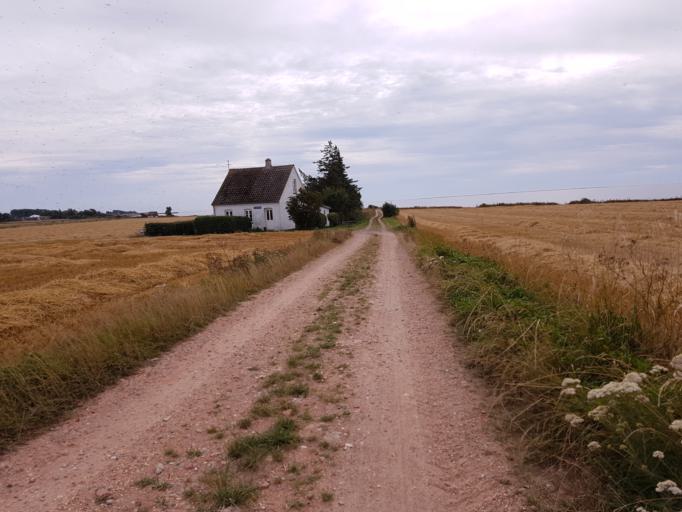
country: DK
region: Zealand
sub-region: Guldborgsund Kommune
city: Nykobing Falster
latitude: 54.5924
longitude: 11.9241
